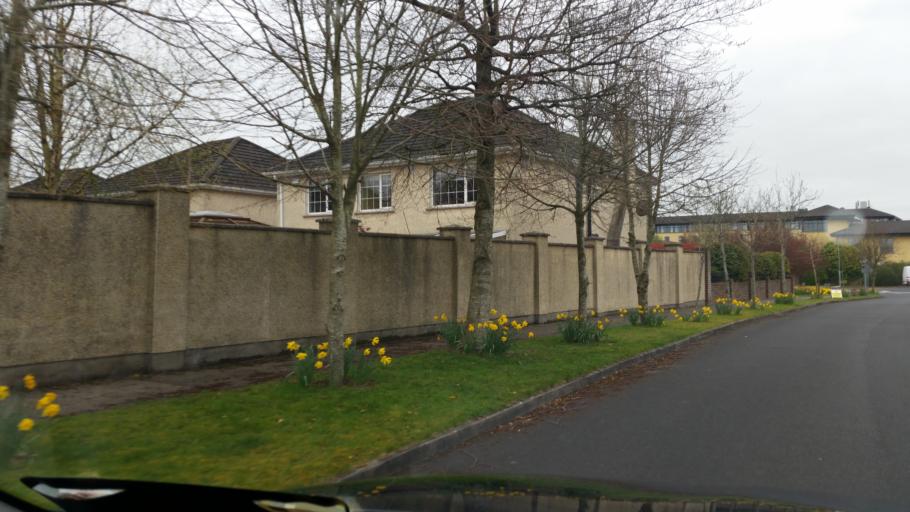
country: IE
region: Leinster
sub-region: An Iarmhi
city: An Muileann gCearr
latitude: 53.5238
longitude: -7.3131
